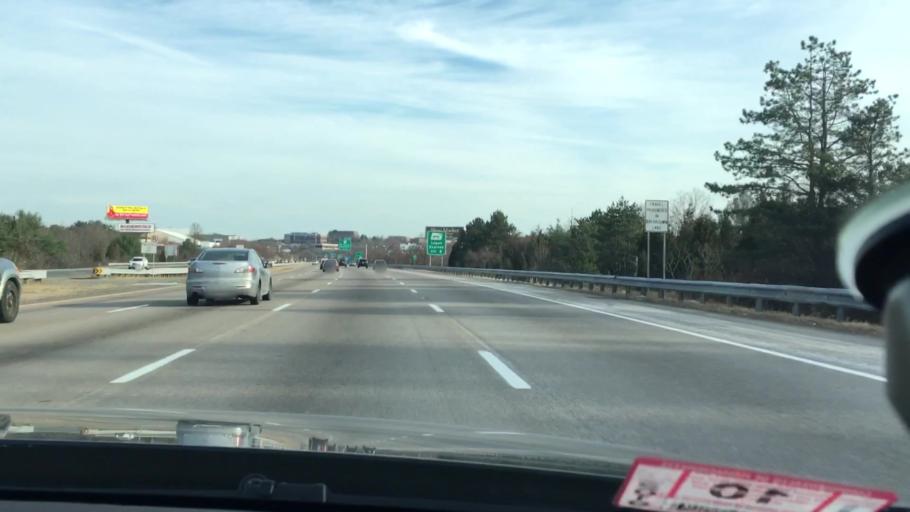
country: US
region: Massachusetts
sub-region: Norfolk County
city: Milton
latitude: 42.2128
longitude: -71.0431
